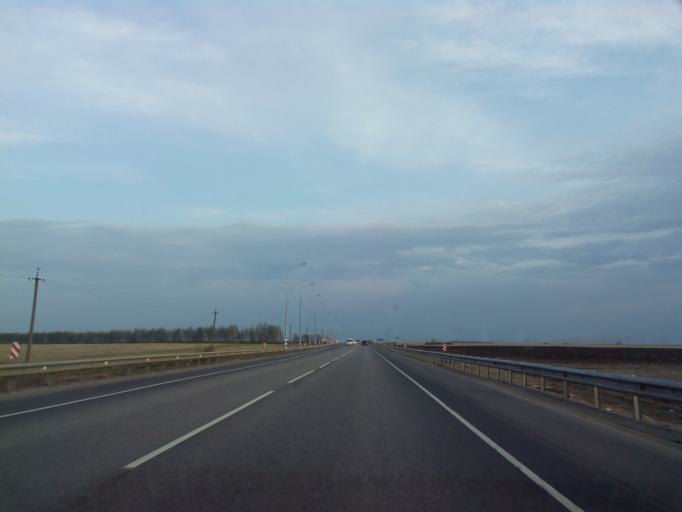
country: RU
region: Rjazan
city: Ryazhsk
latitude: 53.5835
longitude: 40.0411
